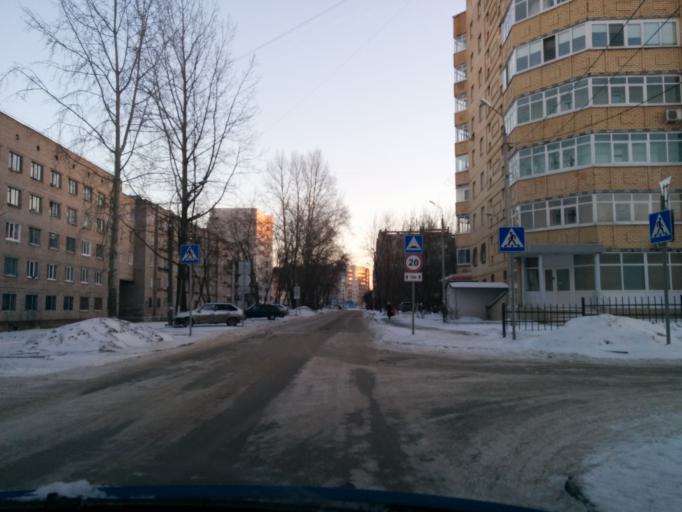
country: RU
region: Perm
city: Perm
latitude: 58.0086
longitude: 56.2672
